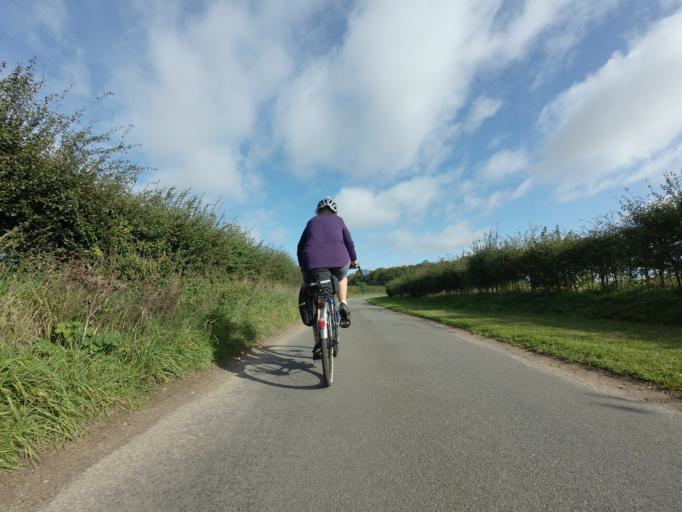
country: GB
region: England
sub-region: Norfolk
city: Fakenham
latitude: 52.8823
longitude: 0.6817
